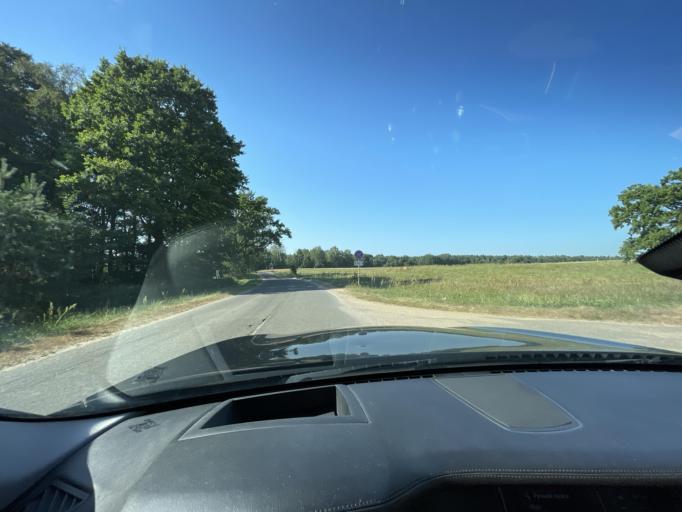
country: BY
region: Grodnenskaya
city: Hrodna
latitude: 53.7591
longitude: 23.9661
